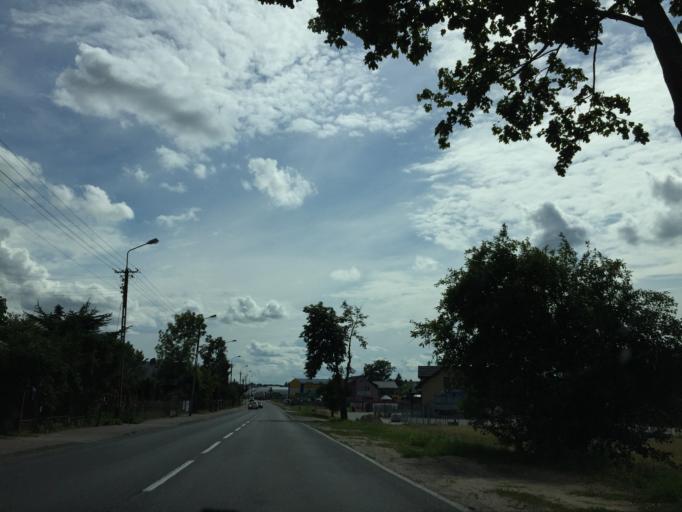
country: PL
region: Masovian Voivodeship
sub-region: Powiat losicki
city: Losice
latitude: 52.2130
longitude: 22.7285
